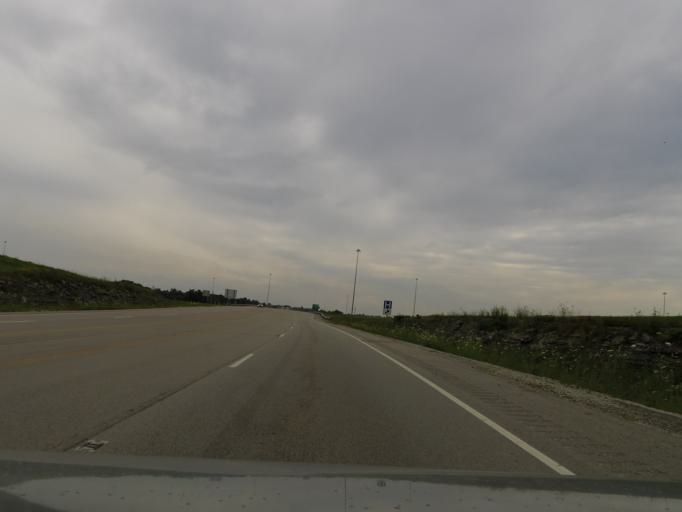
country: US
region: Ohio
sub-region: Brown County
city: Aberdeen
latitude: 38.6456
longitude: -83.8314
